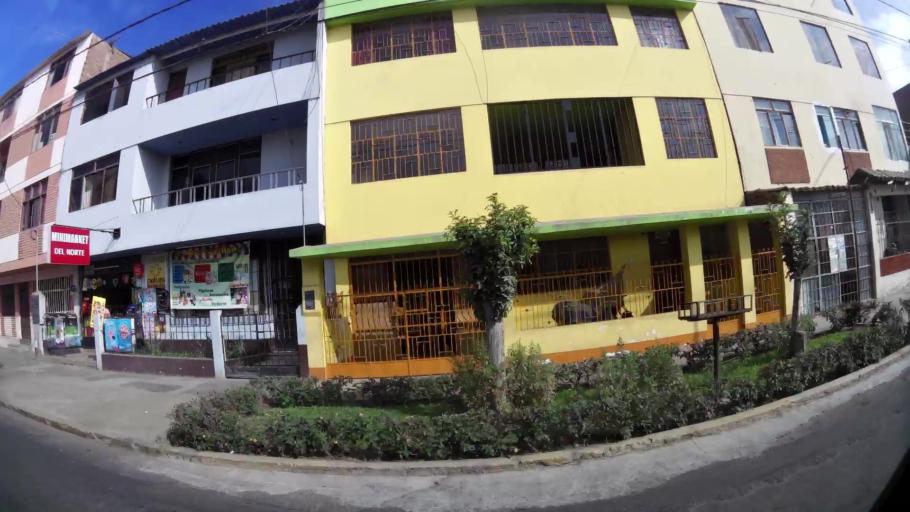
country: PE
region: La Libertad
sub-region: Provincia de Trujillo
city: Trujillo
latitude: -8.1069
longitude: -79.0099
